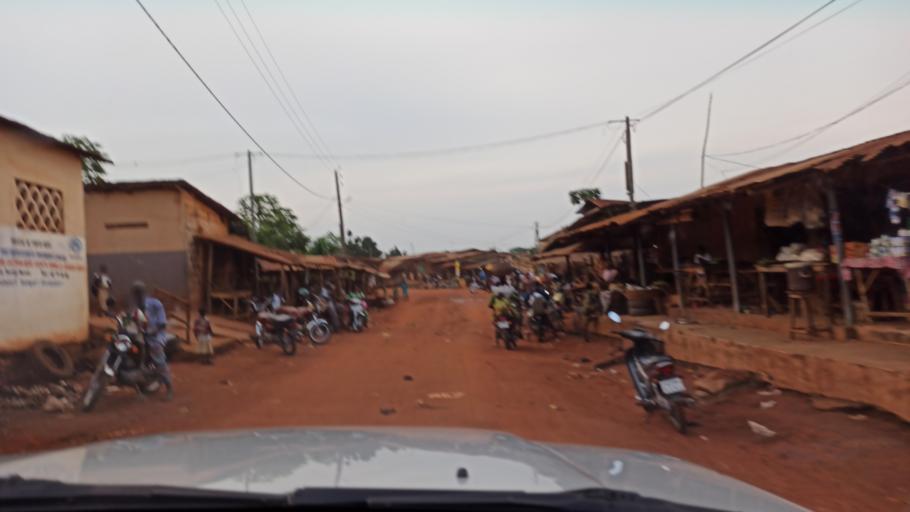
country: BJ
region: Queme
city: Porto-Novo
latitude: 6.5305
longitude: 2.6644
